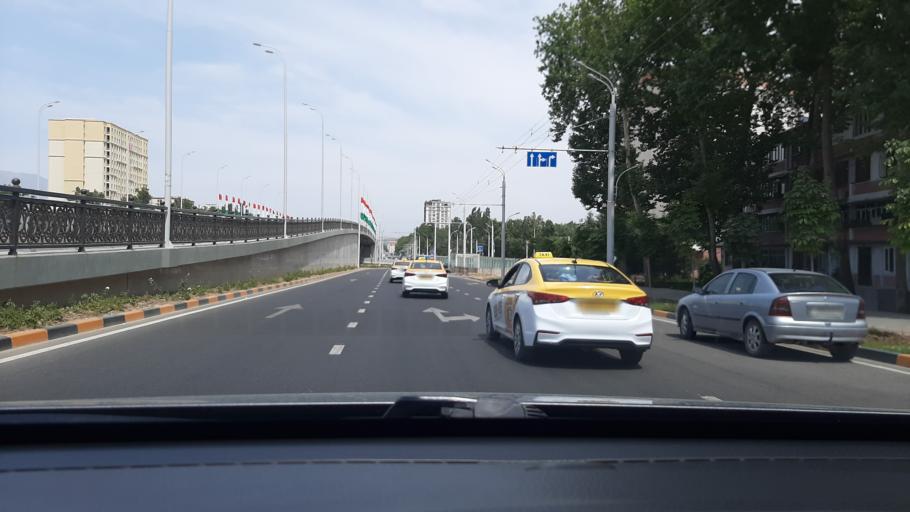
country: TJ
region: Dushanbe
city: Dushanbe
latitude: 38.5829
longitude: 68.7390
